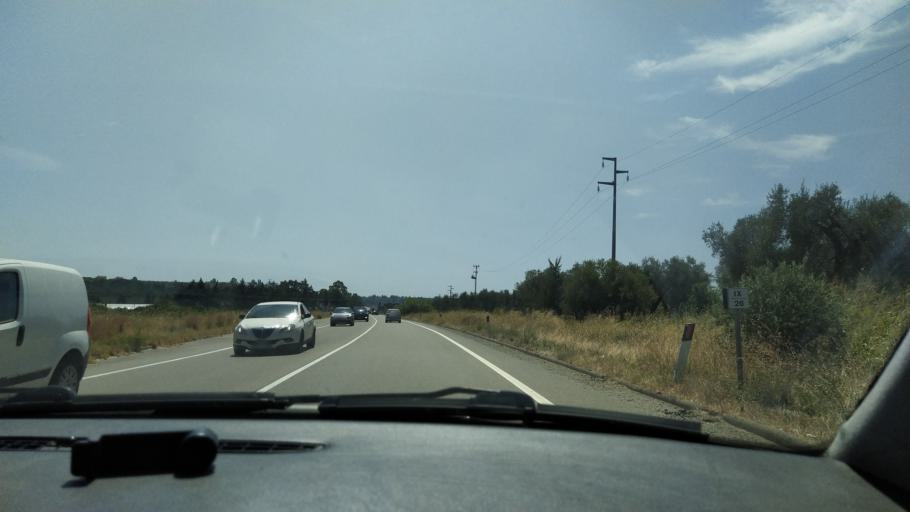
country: IT
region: Basilicate
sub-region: Provincia di Matera
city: Bernalda
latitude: 40.4481
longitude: 16.7765
